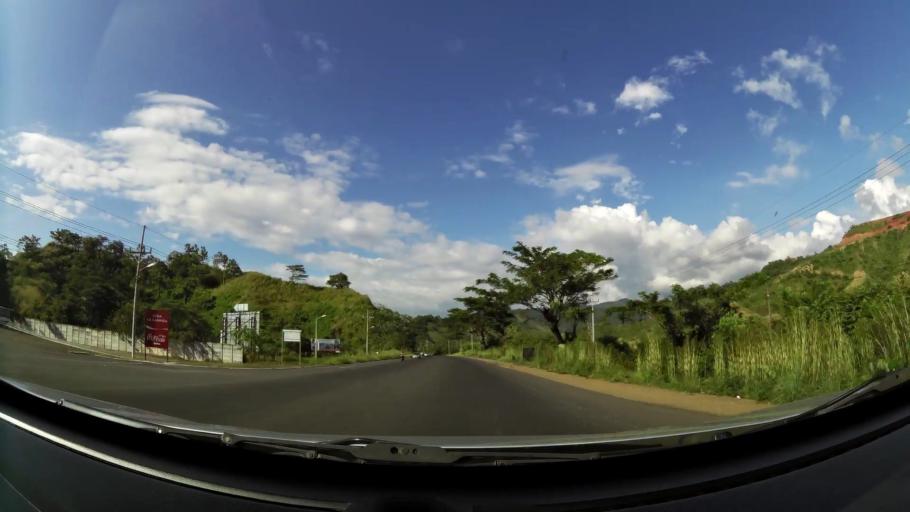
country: CR
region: Puntarenas
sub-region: Canton de Garabito
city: Jaco
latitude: 9.6384
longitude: -84.6272
